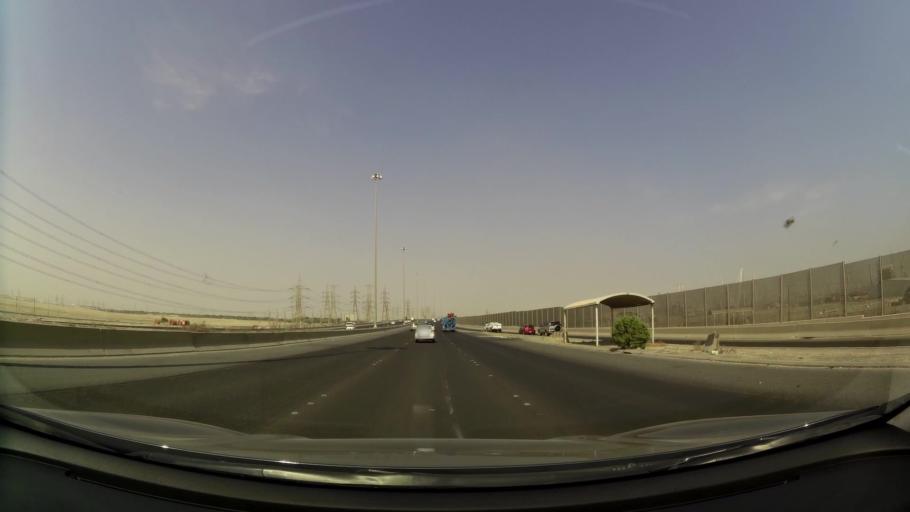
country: KW
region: Al Ahmadi
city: Al Fahahil
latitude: 29.0415
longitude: 48.1160
